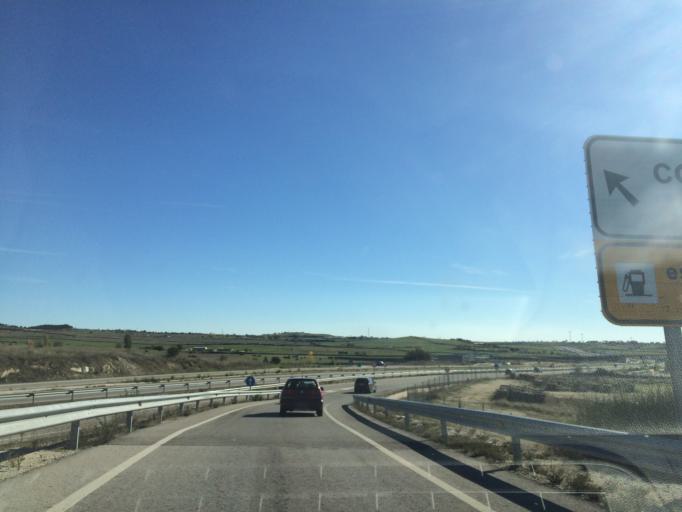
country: ES
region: Madrid
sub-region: Provincia de Madrid
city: Colmenar Viejo
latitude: 40.7206
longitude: -3.7923
